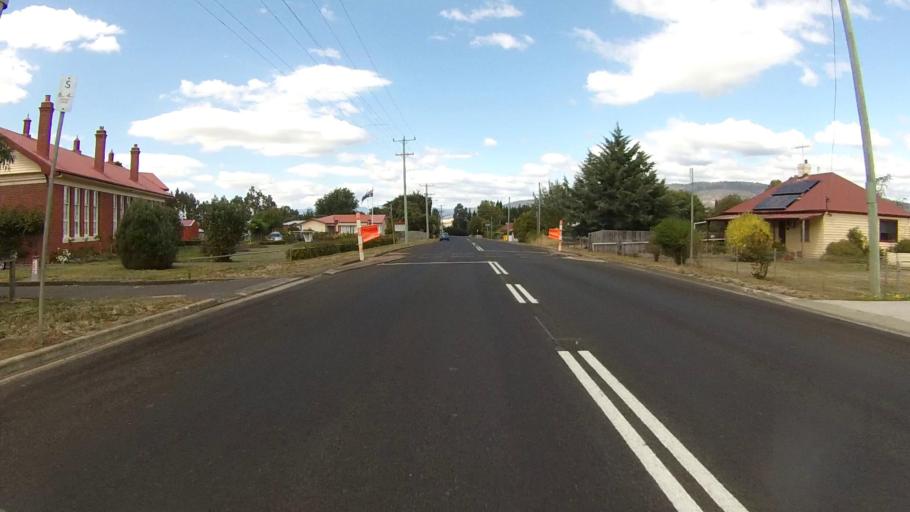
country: AU
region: Tasmania
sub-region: Derwent Valley
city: New Norfolk
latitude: -42.6966
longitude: 146.8889
